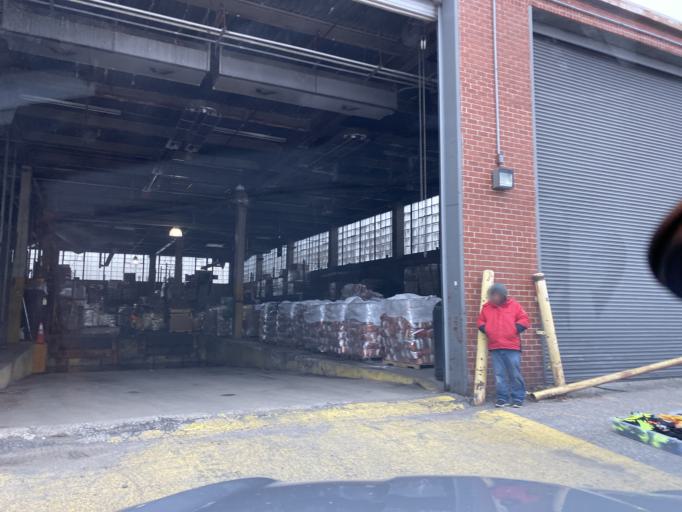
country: US
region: New York
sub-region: Queens County
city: Long Island City
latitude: 40.7261
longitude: -73.9597
